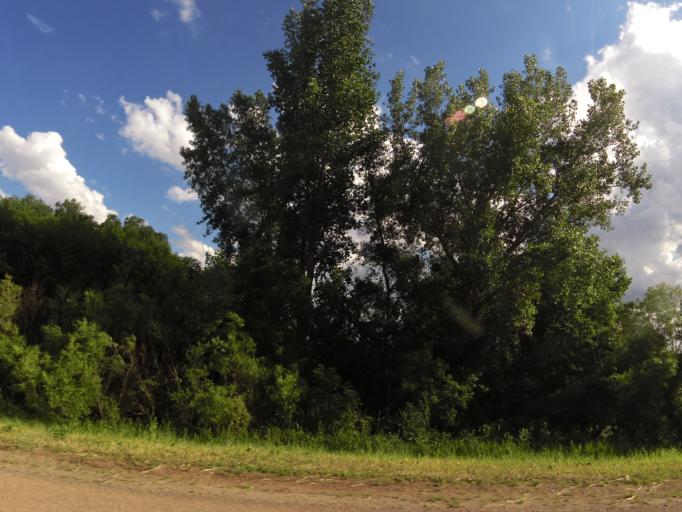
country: US
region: Minnesota
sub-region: Carver County
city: Carver
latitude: 44.8073
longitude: -93.6490
